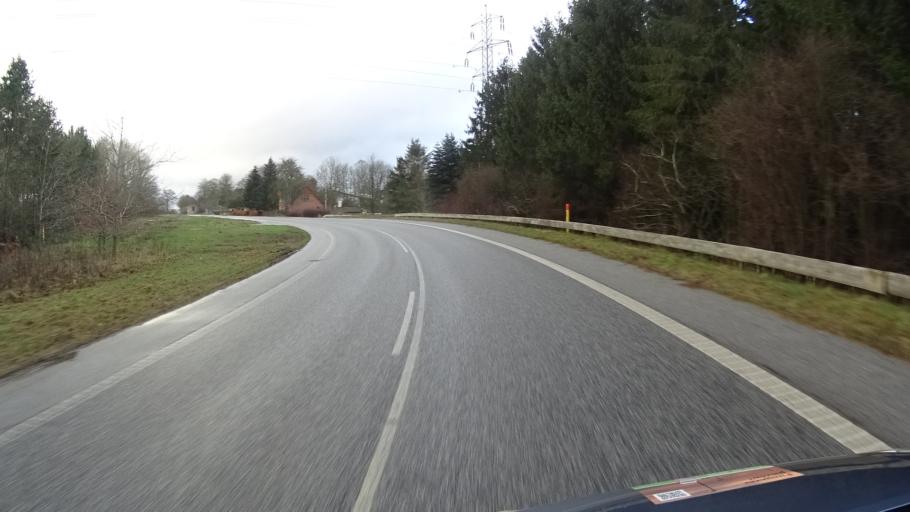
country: DK
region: South Denmark
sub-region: Vejle Kommune
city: Vejle
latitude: 55.7140
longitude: 9.4886
